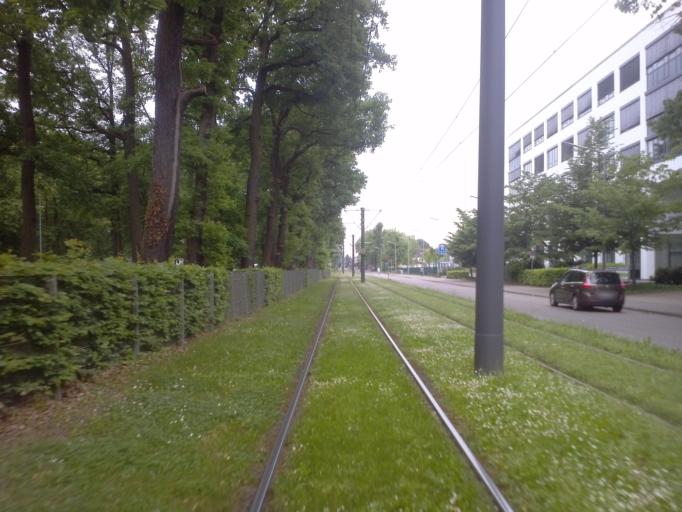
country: DE
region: Baden-Wuerttemberg
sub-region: Karlsruhe Region
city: Karlsruhe
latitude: 49.0261
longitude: 8.3860
